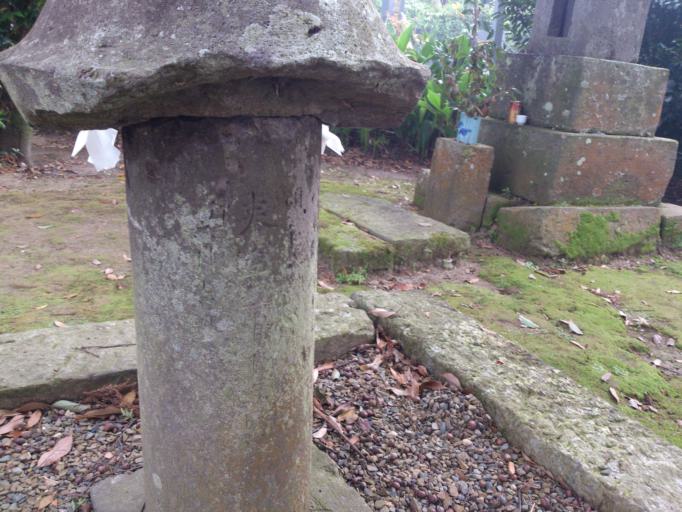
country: JP
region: Kagoshima
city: Kanoya
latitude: 31.3550
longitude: 130.9469
